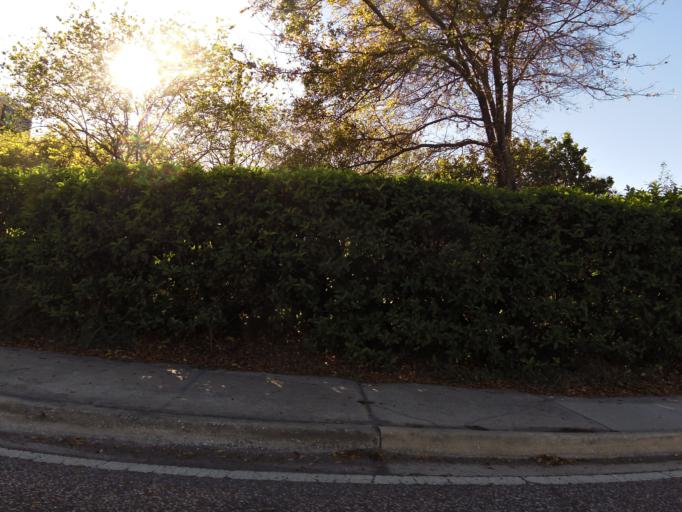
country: US
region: Florida
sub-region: Duval County
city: Jacksonville
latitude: 30.3787
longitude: -81.7685
